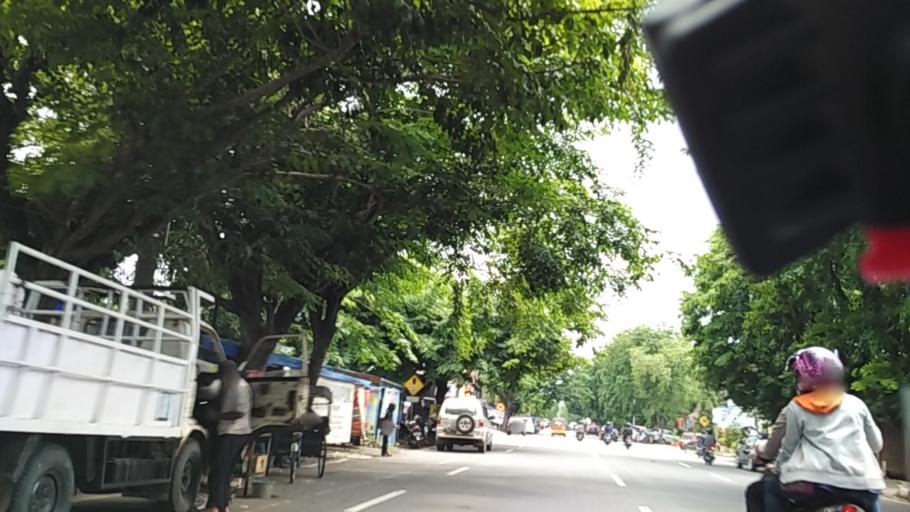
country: ID
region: Central Java
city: Semarang
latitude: -6.9787
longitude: 110.4352
